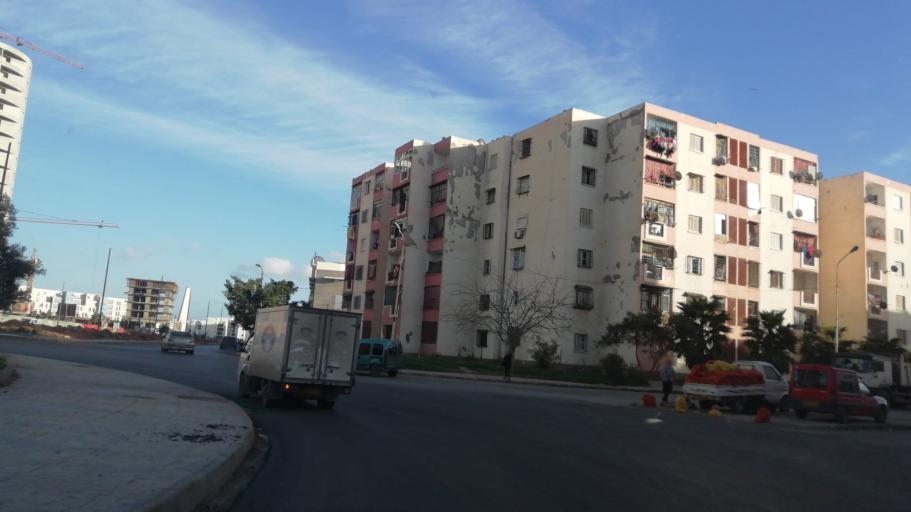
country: DZ
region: Oran
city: Bir el Djir
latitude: 35.7082
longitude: -0.5631
